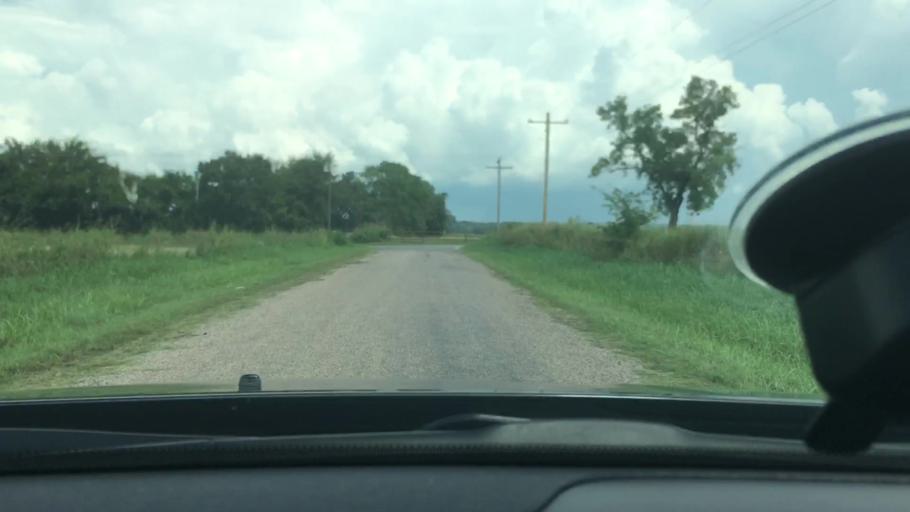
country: US
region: Oklahoma
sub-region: Carter County
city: Dickson
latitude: 34.2262
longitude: -96.8982
